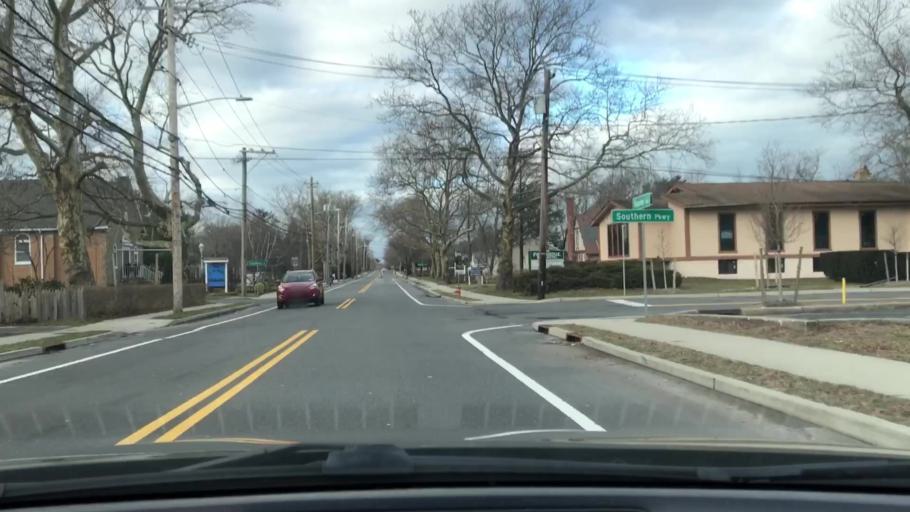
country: US
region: New York
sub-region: Suffolk County
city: Riverhead
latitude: 40.9274
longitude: -72.6694
